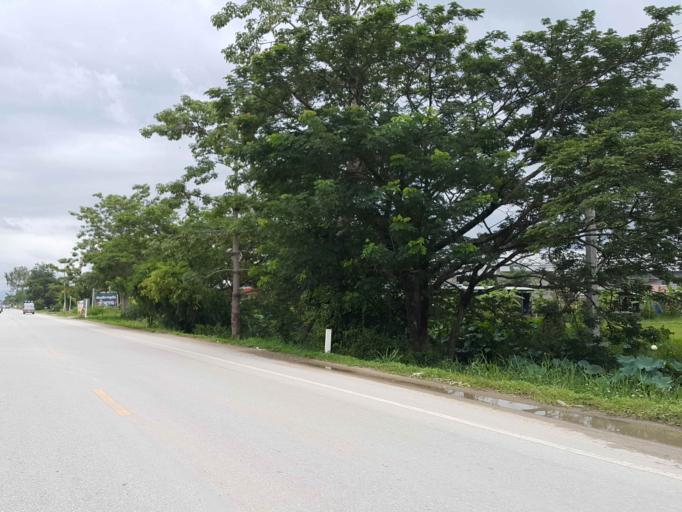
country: TH
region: Chiang Mai
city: San Sai
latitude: 18.8105
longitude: 99.0573
